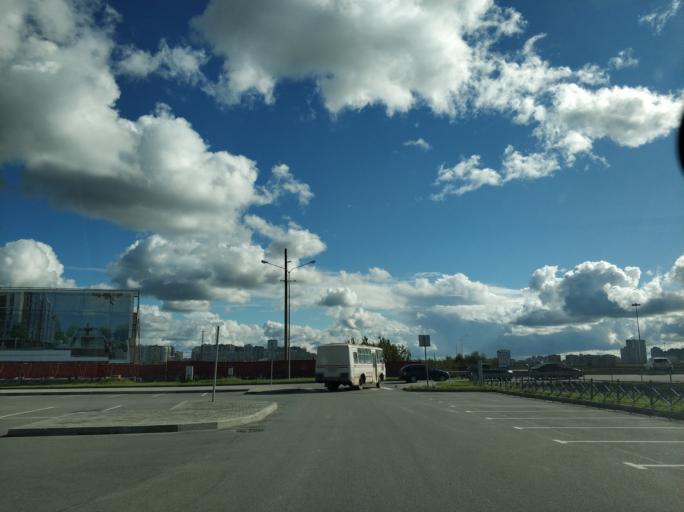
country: RU
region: Leningrad
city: Bugry
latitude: 60.0599
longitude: 30.3922
